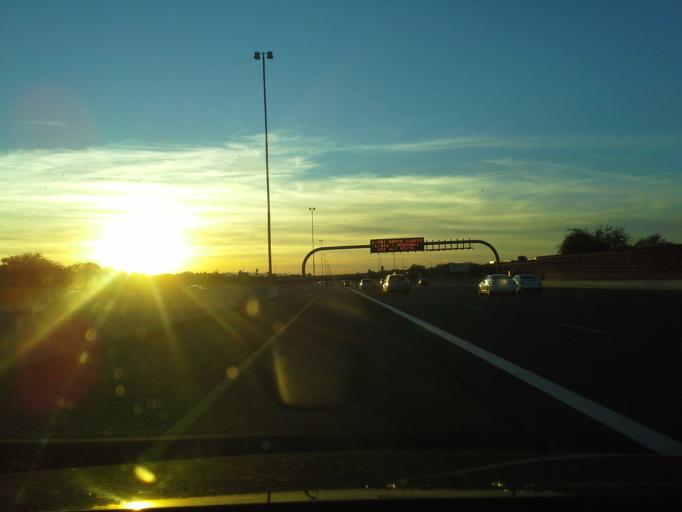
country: US
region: Arizona
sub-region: Pinal County
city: Apache Junction
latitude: 33.3867
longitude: -111.6626
